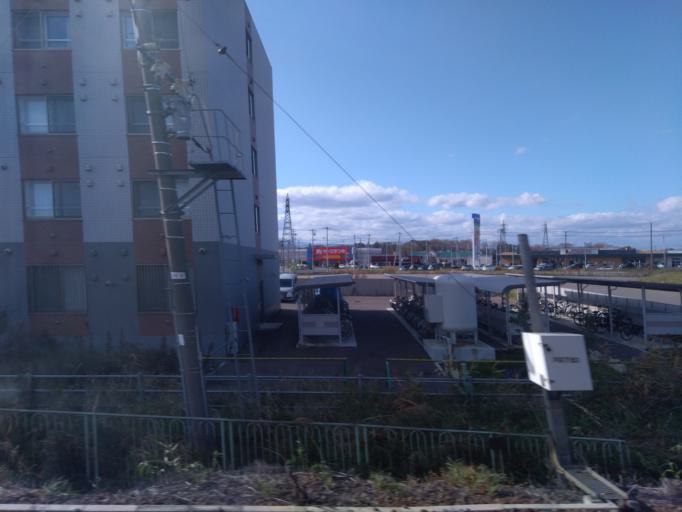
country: JP
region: Hokkaido
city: Kitahiroshima
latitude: 42.9037
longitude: 141.5744
